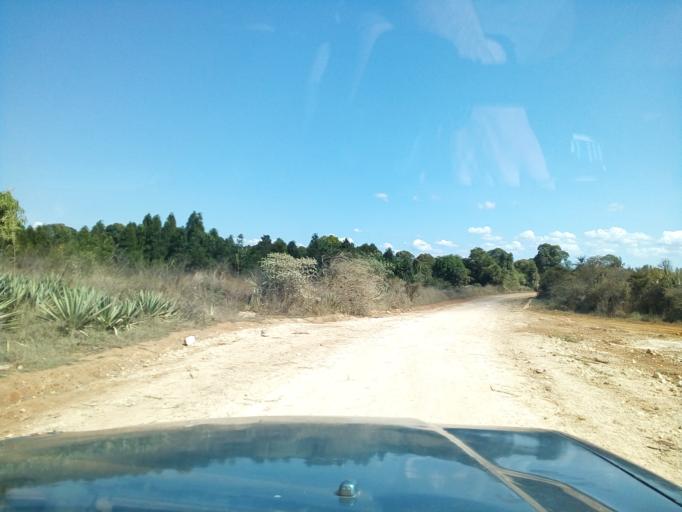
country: MG
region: Boeny
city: Mahajanga
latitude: -15.9611
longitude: 45.9651
